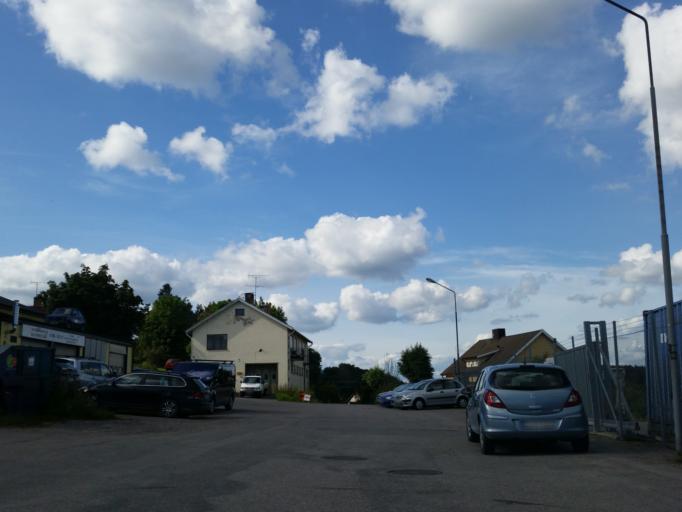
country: SE
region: Soedermanland
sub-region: Trosa Kommun
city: Vagnharad
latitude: 58.9476
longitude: 17.5018
